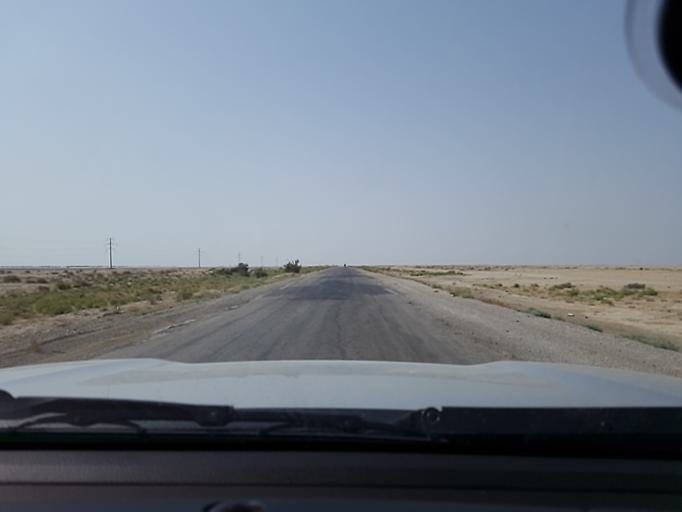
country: TM
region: Balkan
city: Gumdag
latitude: 38.8817
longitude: 54.5935
